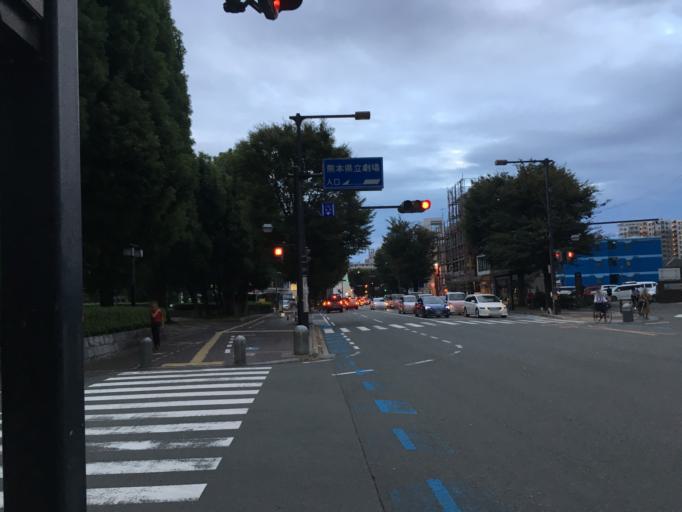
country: JP
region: Kumamoto
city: Kumamoto
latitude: 32.8023
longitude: 130.7270
